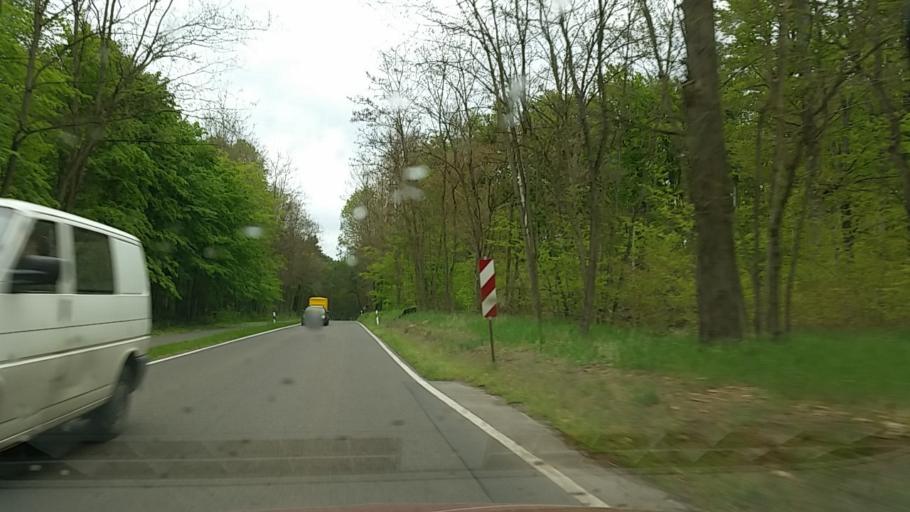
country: DE
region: Brandenburg
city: Reichenwalde
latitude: 52.3083
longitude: 13.9690
